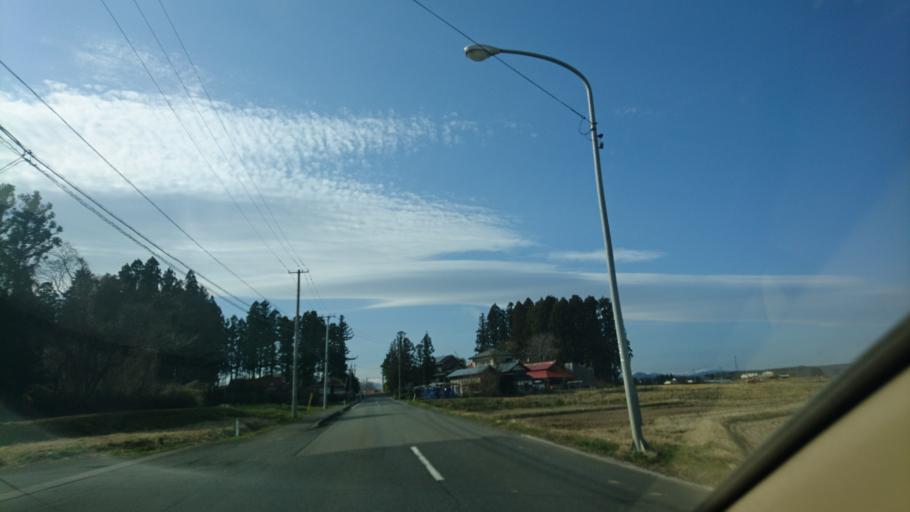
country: JP
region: Iwate
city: Ichinoseki
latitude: 38.8002
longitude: 141.0473
